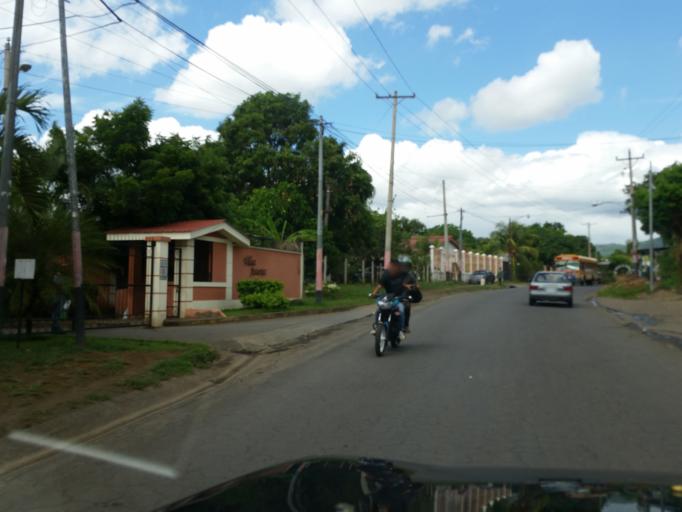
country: NI
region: Masaya
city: Ticuantepe
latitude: 12.0596
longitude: -86.1944
